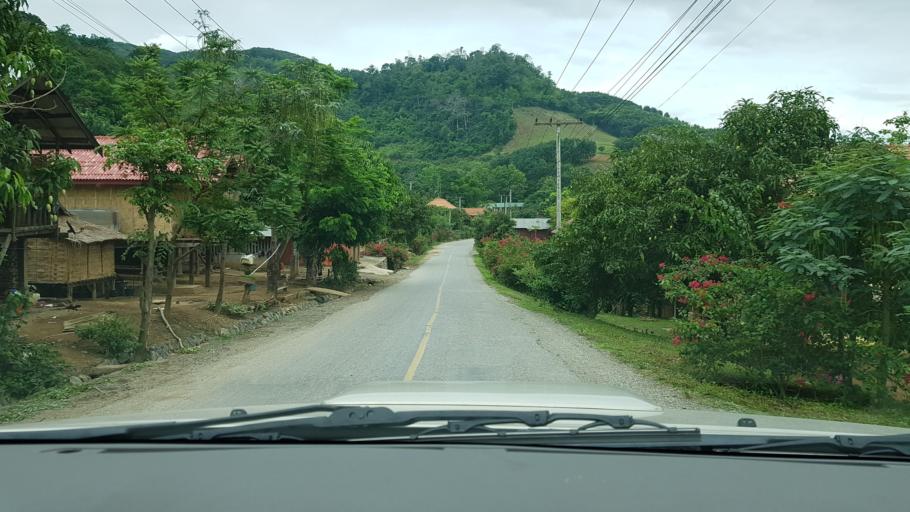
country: LA
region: Loungnamtha
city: Muang Nale
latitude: 20.1723
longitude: 101.5121
